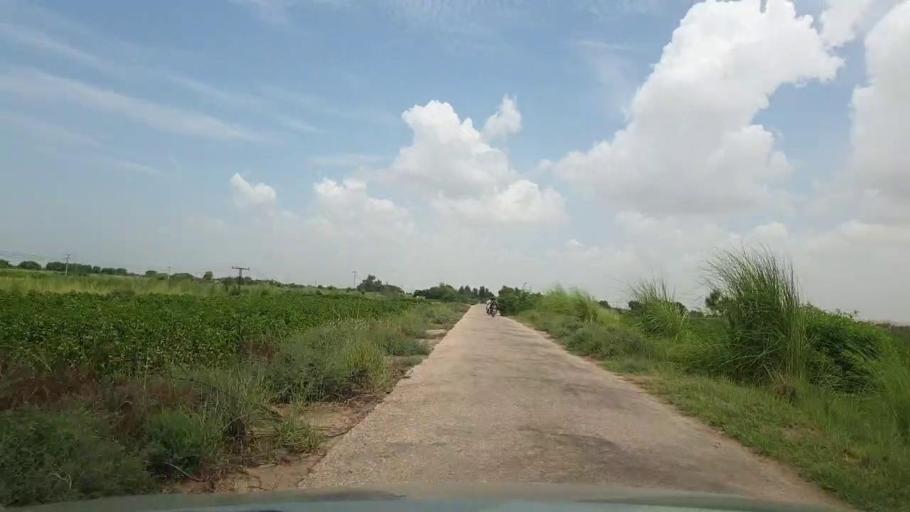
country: PK
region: Sindh
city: Bozdar
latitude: 27.0191
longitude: 68.9438
